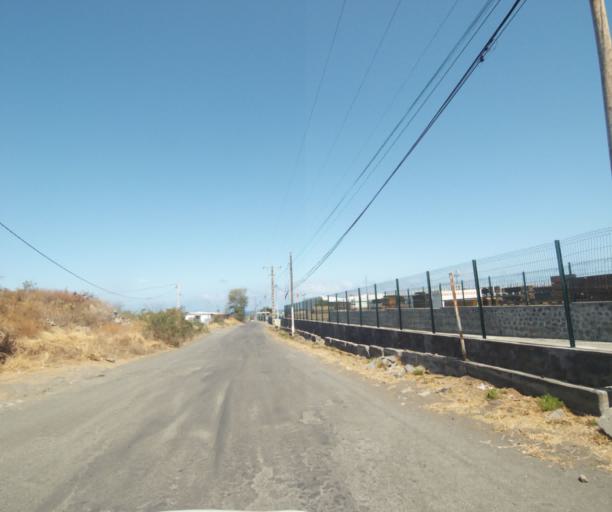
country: RE
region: Reunion
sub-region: Reunion
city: Le Port
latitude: -20.9637
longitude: 55.2889
